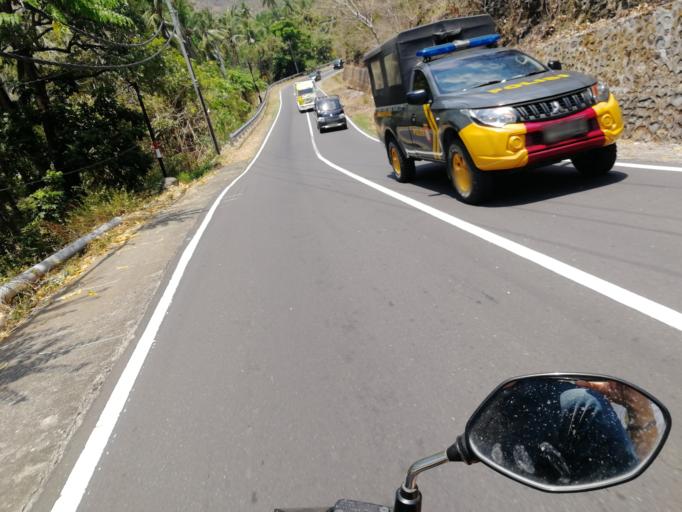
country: ID
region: West Nusa Tenggara
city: Karangsubagan
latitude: -8.4438
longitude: 116.0364
